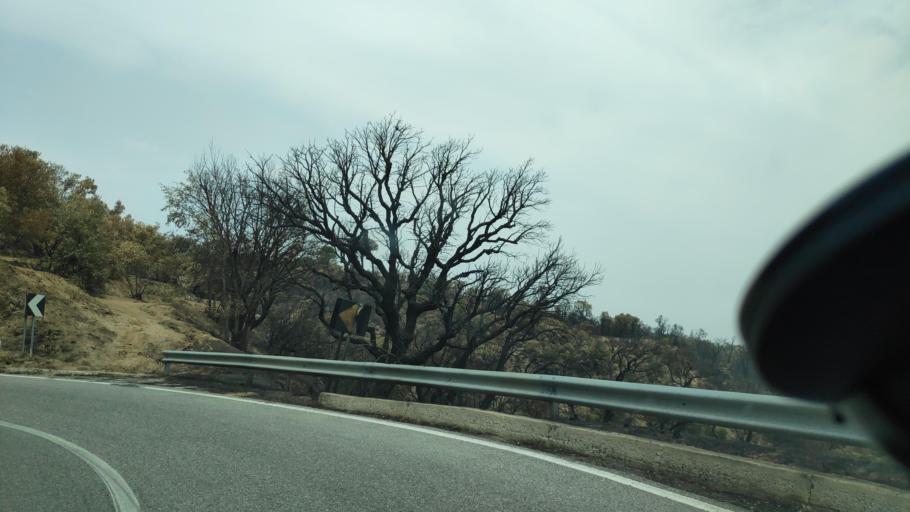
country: IT
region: Calabria
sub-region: Provincia di Catanzaro
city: Sant'Andrea Apostolo dello Ionio
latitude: 38.6408
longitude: 16.5213
